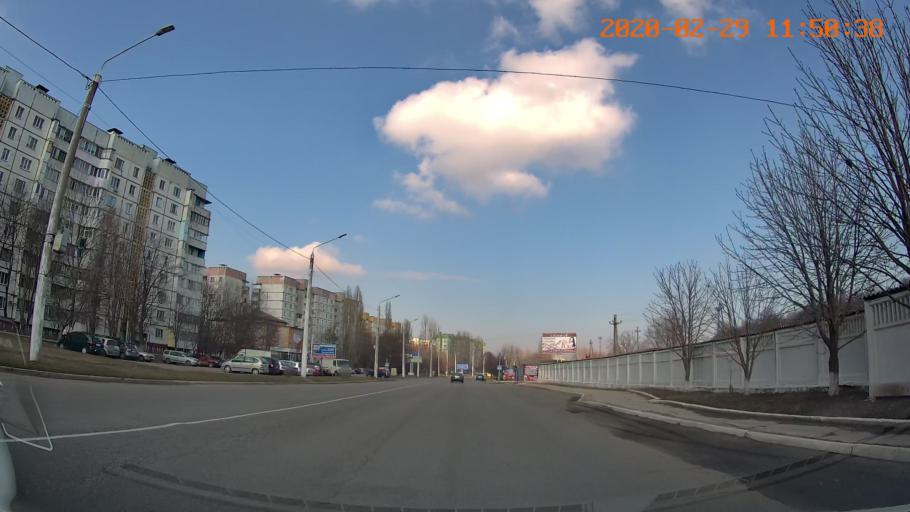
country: MD
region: Telenesti
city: Ribnita
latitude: 47.7595
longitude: 28.9902
